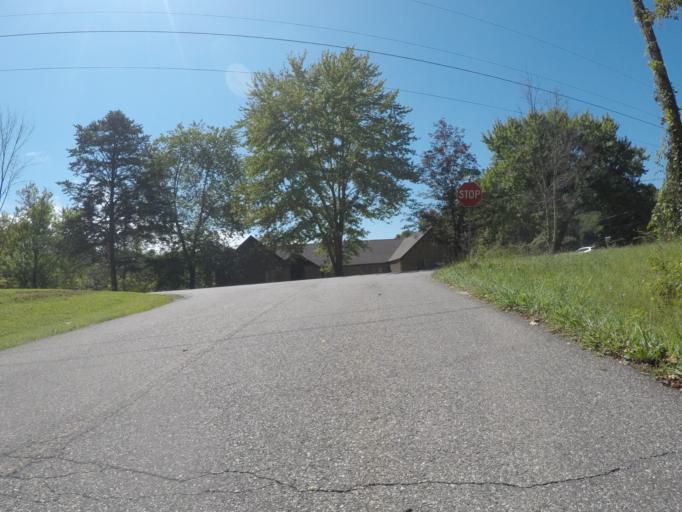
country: US
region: Kentucky
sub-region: Boyd County
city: Meads
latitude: 38.4185
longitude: -82.6632
